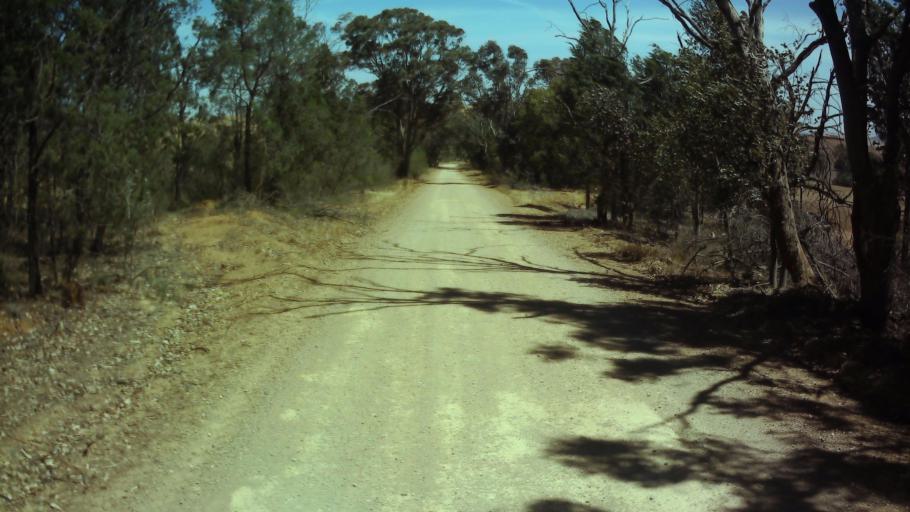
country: AU
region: New South Wales
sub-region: Weddin
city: Grenfell
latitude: -33.9197
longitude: 148.1788
